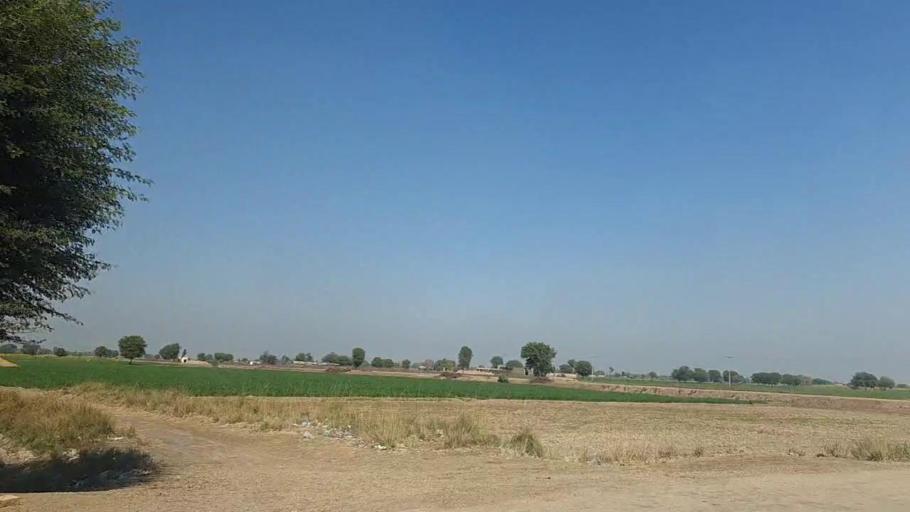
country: PK
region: Sindh
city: Shahpur Chakar
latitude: 26.1972
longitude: 68.5657
